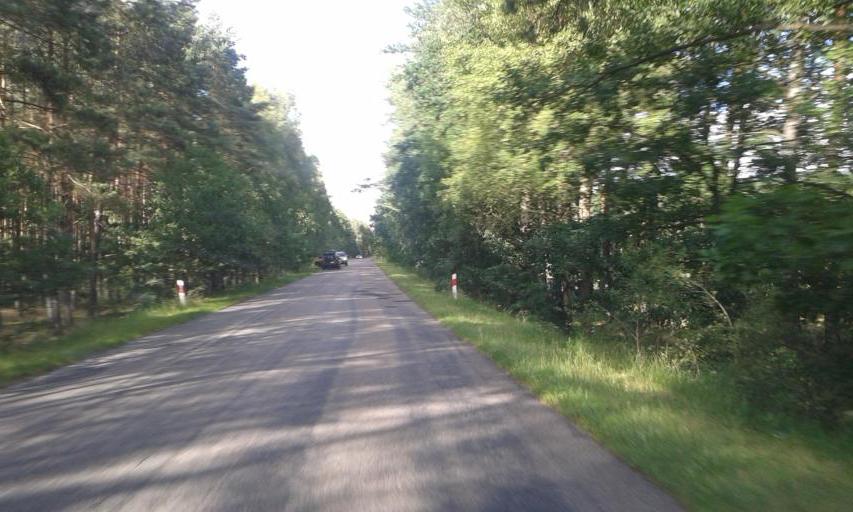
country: PL
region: West Pomeranian Voivodeship
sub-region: Powiat szczecinecki
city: Barwice
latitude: 53.6641
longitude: 16.3357
